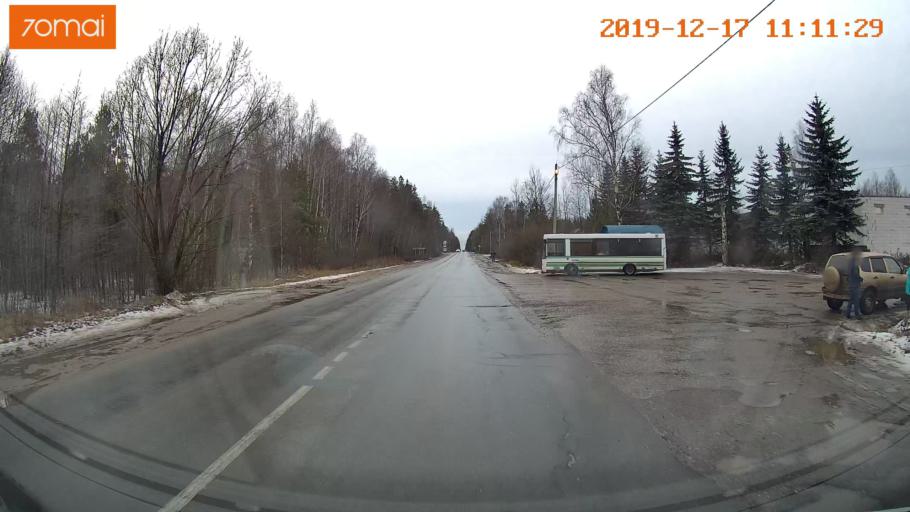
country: RU
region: Vladimir
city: Gus'-Khrustal'nyy
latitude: 55.5861
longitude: 40.6364
